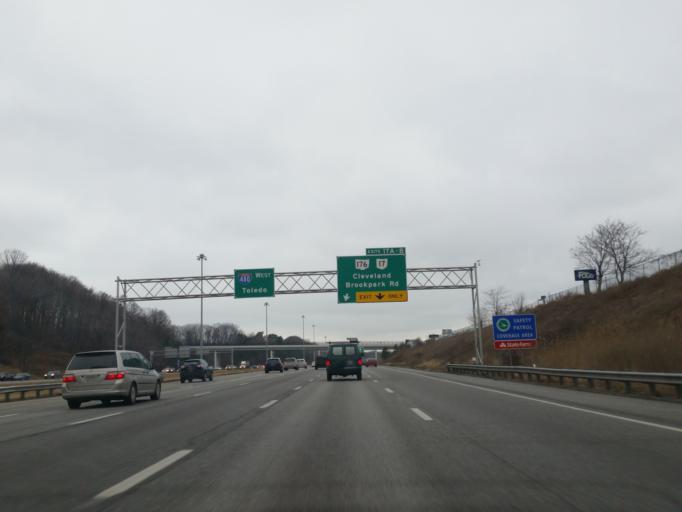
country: US
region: Ohio
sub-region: Cuyahoga County
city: Seven Hills
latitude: 41.4101
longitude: -81.6614
